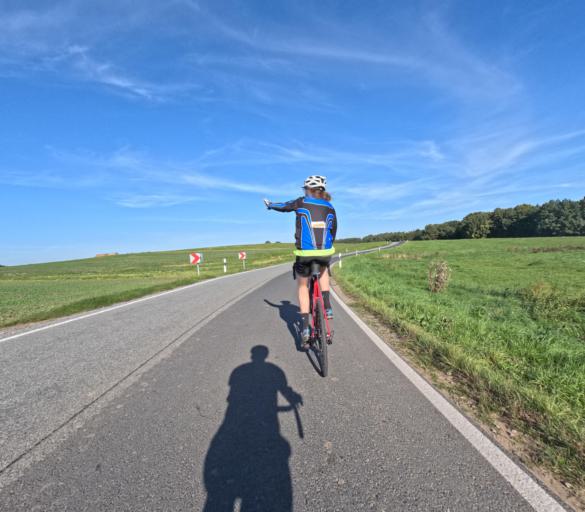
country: DE
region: Saxony
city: Ottendorf-Okrilla
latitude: 51.1408
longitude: 13.8393
